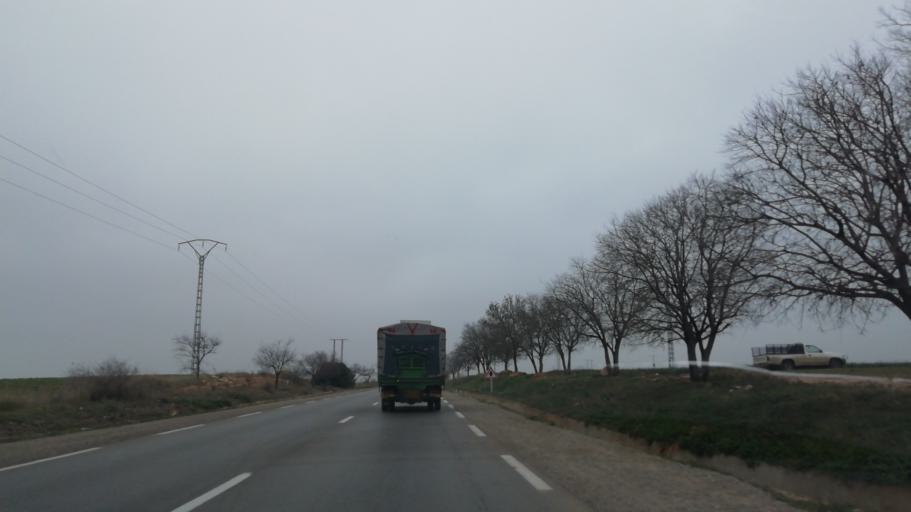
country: DZ
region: Mascara
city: Mascara
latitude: 35.3168
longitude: 0.3753
